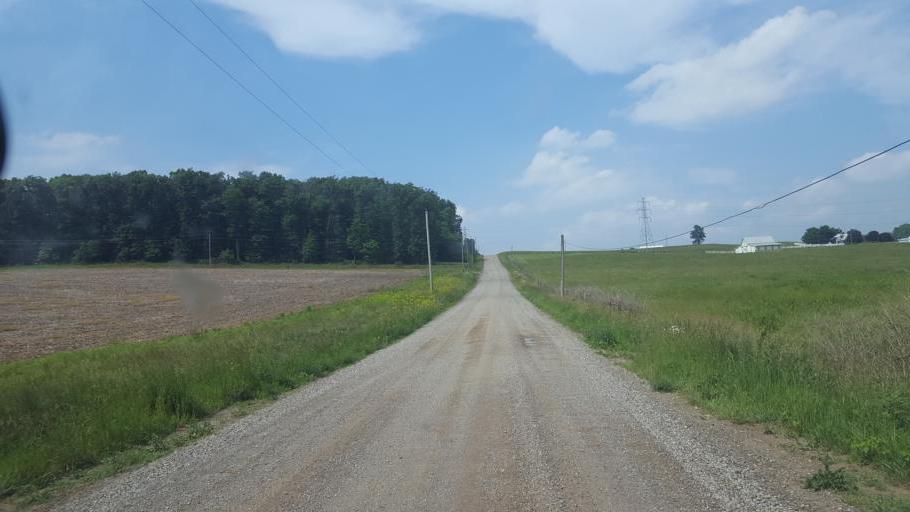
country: US
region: Ohio
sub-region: Knox County
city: Oak Hill
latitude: 40.2917
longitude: -82.2129
